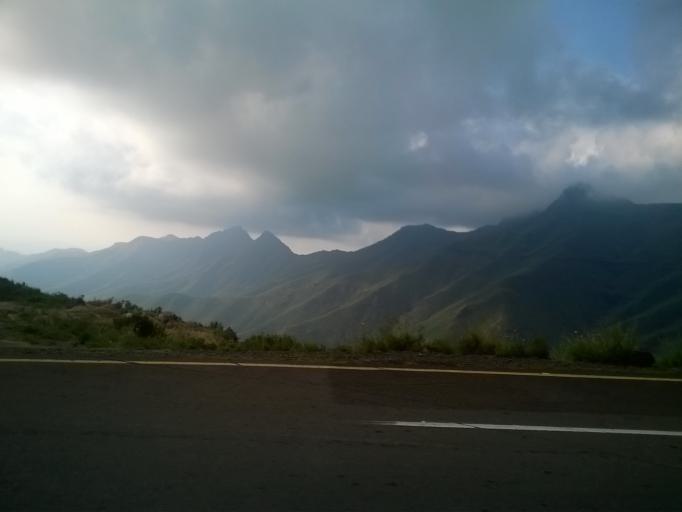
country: LS
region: Butha-Buthe
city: Butha-Buthe
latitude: -29.0688
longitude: 28.3802
